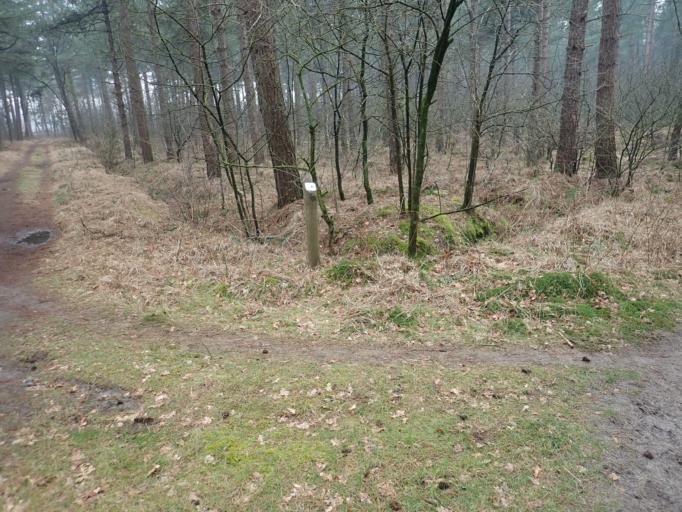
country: BE
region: Flanders
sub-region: Provincie Antwerpen
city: Essen
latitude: 51.4802
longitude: 4.5224
